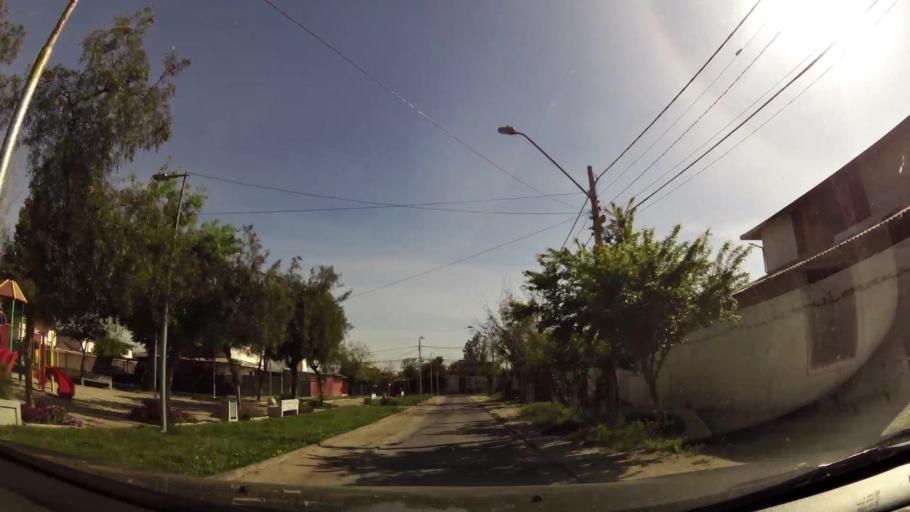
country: CL
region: Santiago Metropolitan
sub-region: Provincia de Cordillera
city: Puente Alto
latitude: -33.6074
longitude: -70.5879
